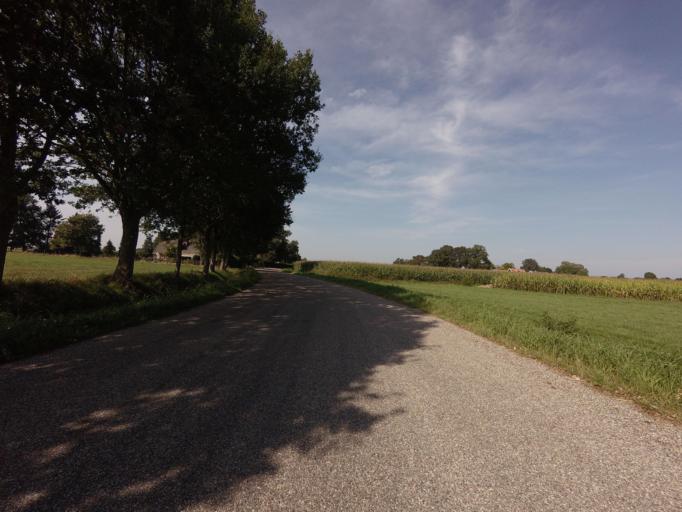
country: NL
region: Overijssel
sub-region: Gemeente Hof van Twente
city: Goor
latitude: 52.2505
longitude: 6.6331
